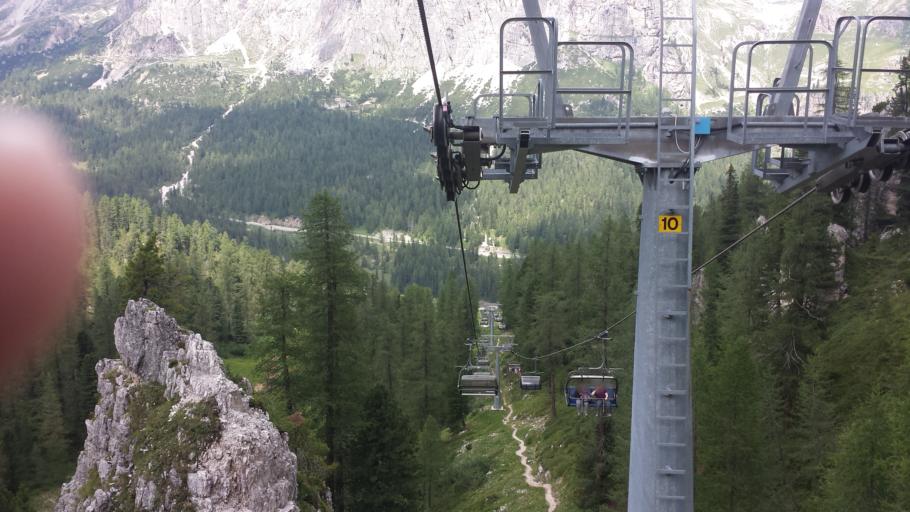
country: IT
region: Veneto
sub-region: Provincia di Belluno
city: Selva di Cadore
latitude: 46.5126
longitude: 12.0432
